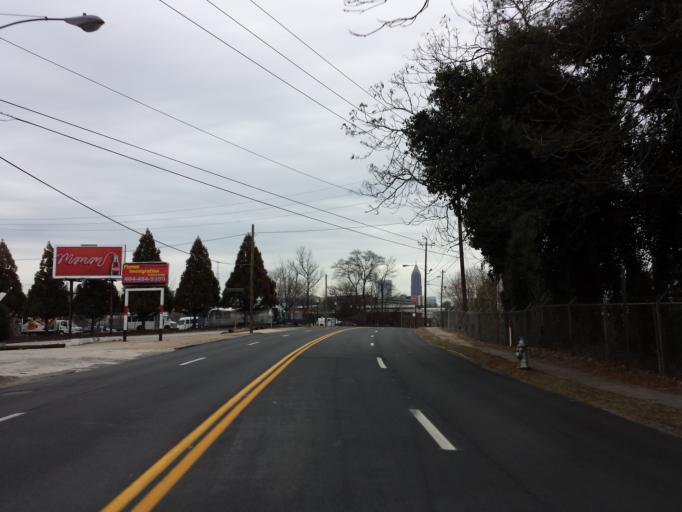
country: US
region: Georgia
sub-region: Fulton County
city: Atlanta
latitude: 33.7849
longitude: -84.4202
